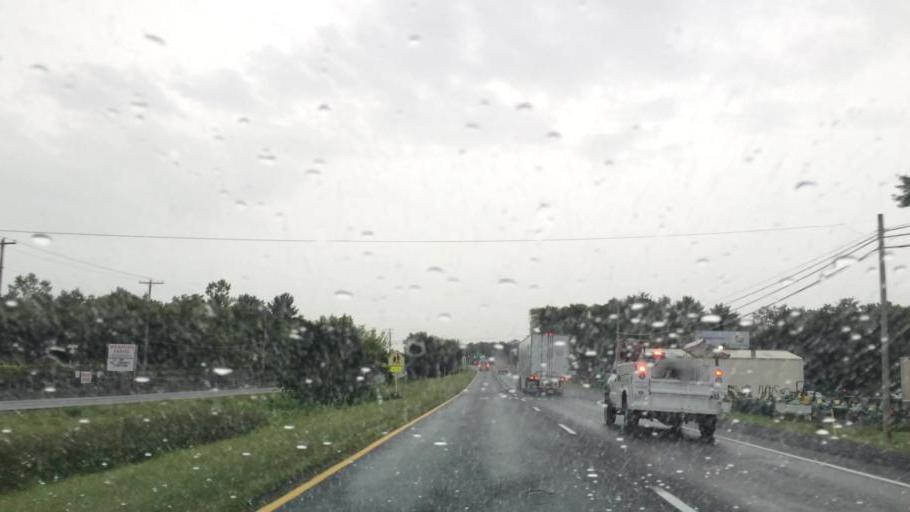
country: US
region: Virginia
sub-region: City of Winchester
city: Winchester
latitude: 39.1868
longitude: -78.1248
